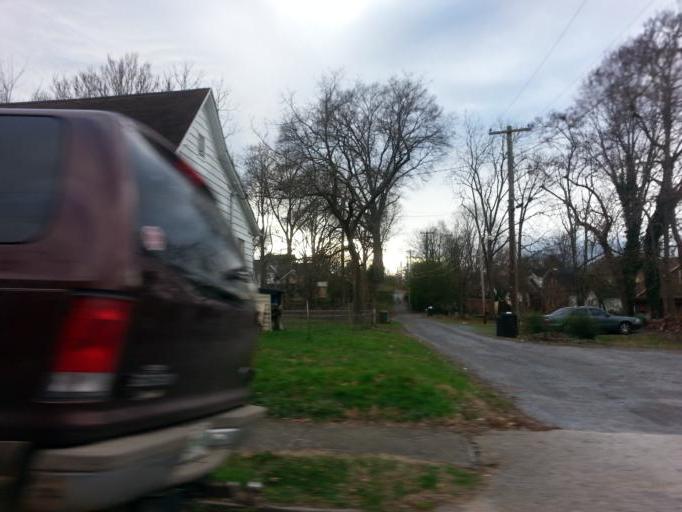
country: US
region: Tennessee
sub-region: Washington County
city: Johnson City
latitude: 36.3105
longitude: -82.3514
